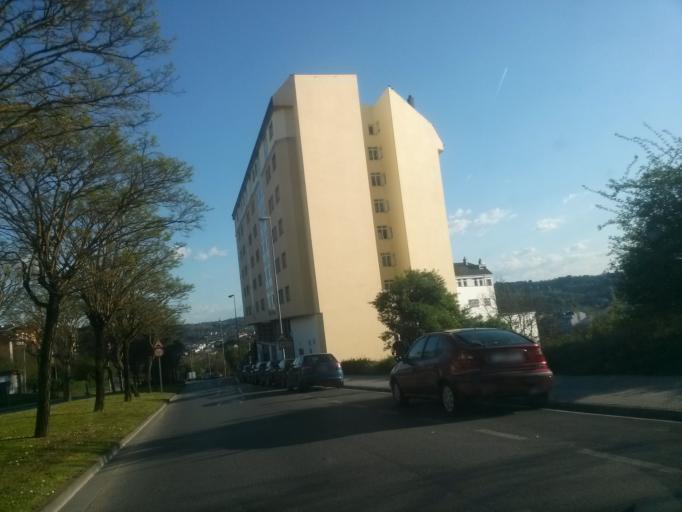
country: ES
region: Galicia
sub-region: Provincia de Lugo
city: Lugo
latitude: 43.0095
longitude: -7.5657
